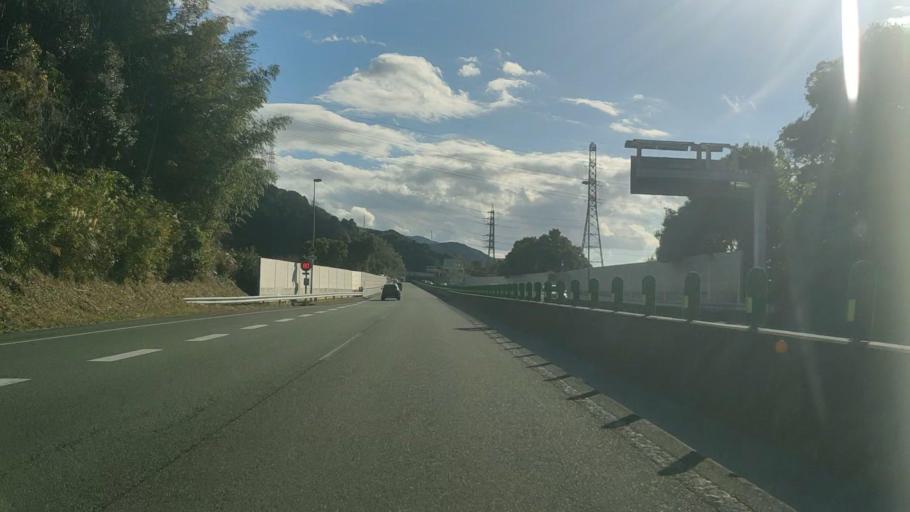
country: JP
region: Fukuoka
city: Kitakyushu
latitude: 33.8382
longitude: 130.7654
